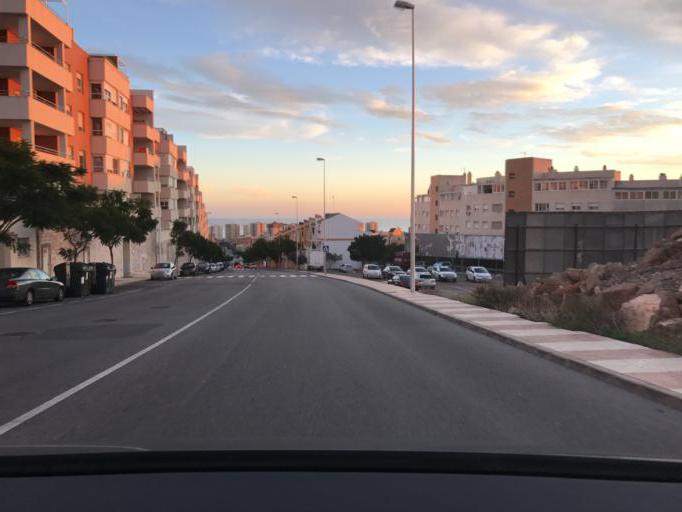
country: ES
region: Andalusia
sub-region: Provincia de Almeria
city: Aguadulce
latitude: 36.8206
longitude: -2.5827
